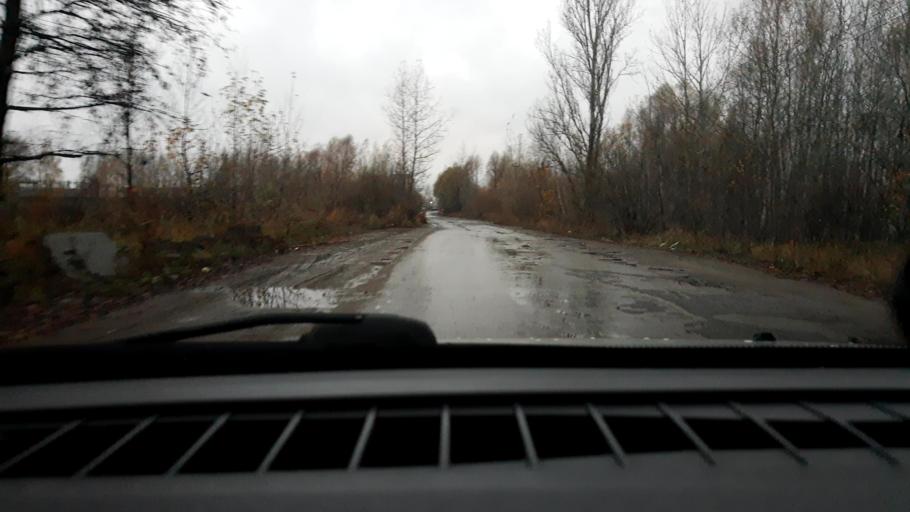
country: RU
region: Nizjnij Novgorod
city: Gorbatovka
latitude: 56.2681
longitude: 43.8568
